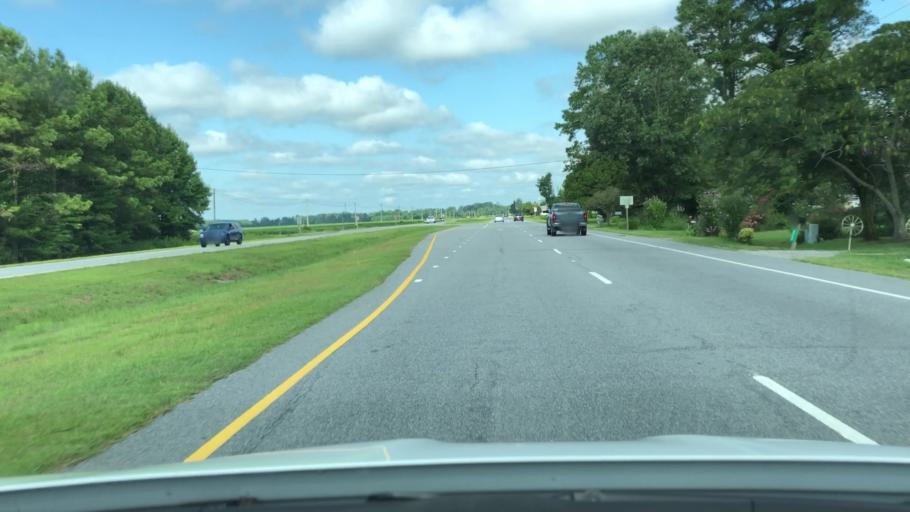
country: US
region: North Carolina
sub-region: Perquimans County
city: Hertford
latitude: 36.2078
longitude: -76.4064
